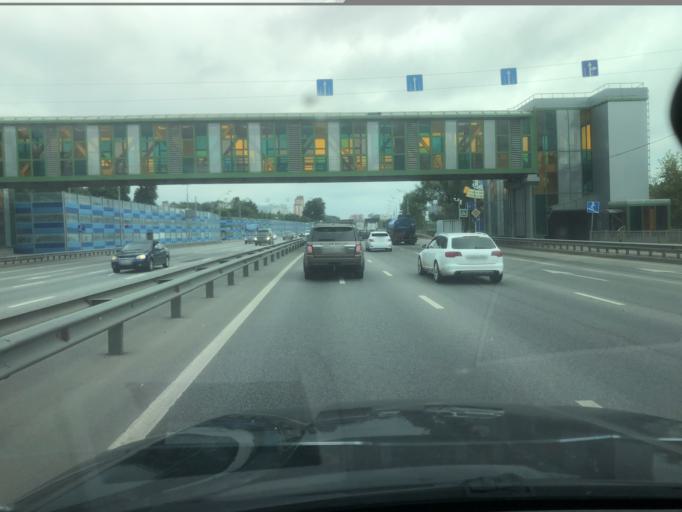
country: RU
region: Moscow
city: Severnyy
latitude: 55.9434
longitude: 37.5431
